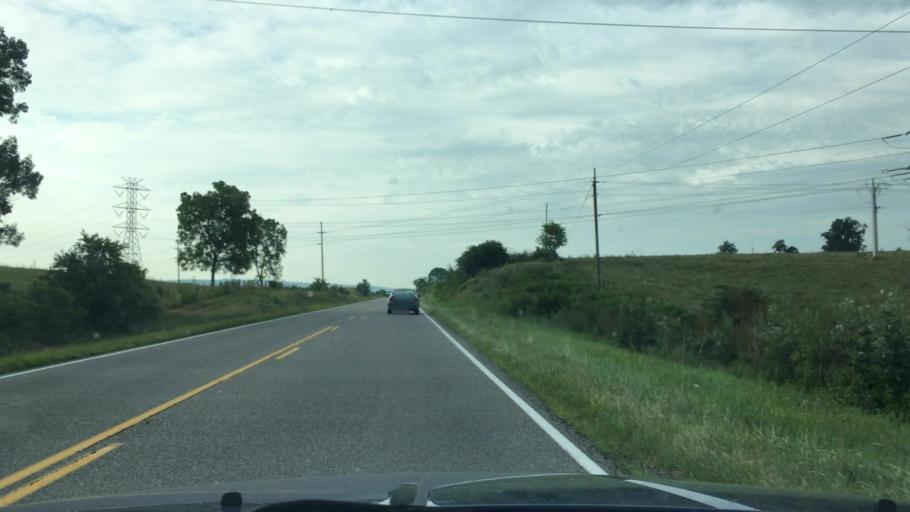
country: US
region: Virginia
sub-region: Augusta County
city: Dooms
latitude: 38.1220
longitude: -78.9130
